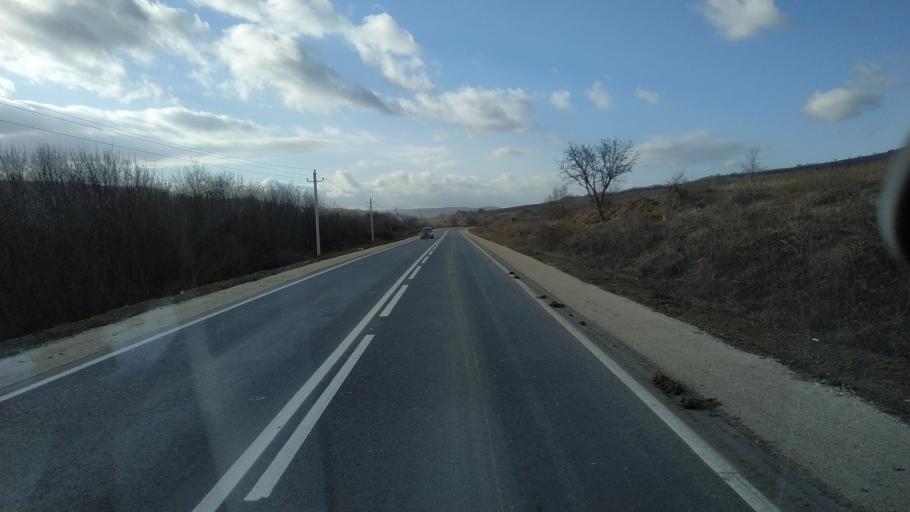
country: MD
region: Calarasi
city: Calarasi
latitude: 47.2921
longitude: 28.1768
